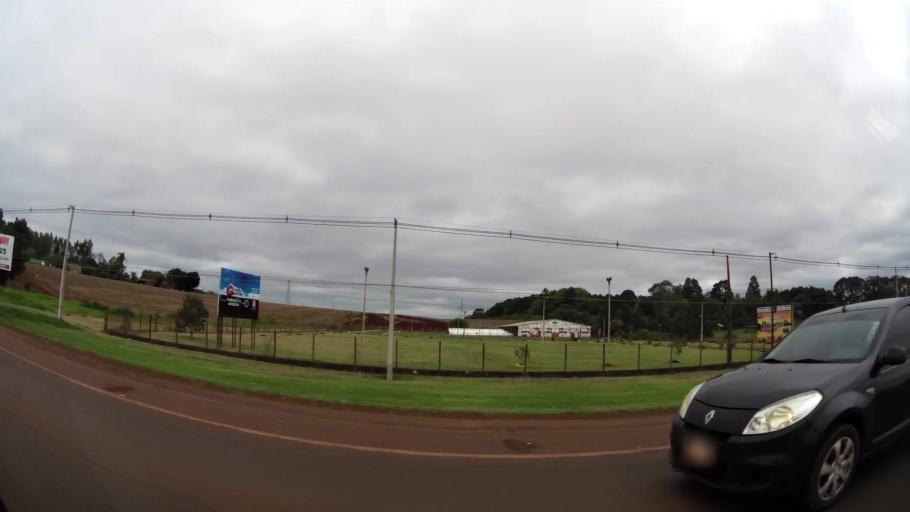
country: PY
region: Alto Parana
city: Presidente Franco
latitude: -25.4907
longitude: -54.7701
